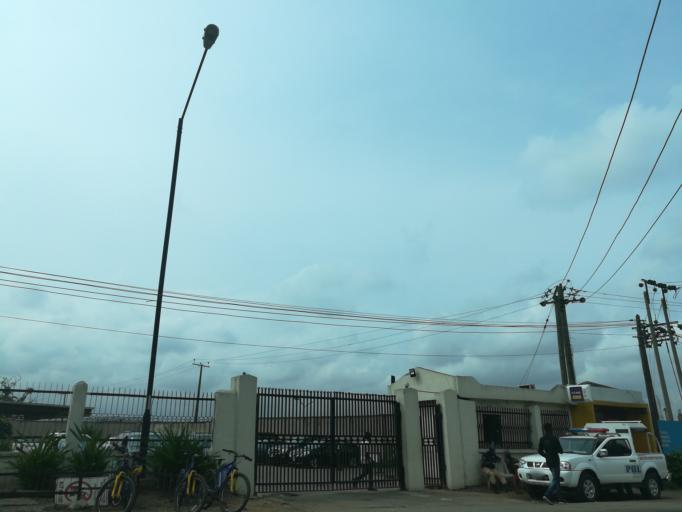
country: NG
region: Lagos
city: Ojota
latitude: 6.5996
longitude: 3.3753
